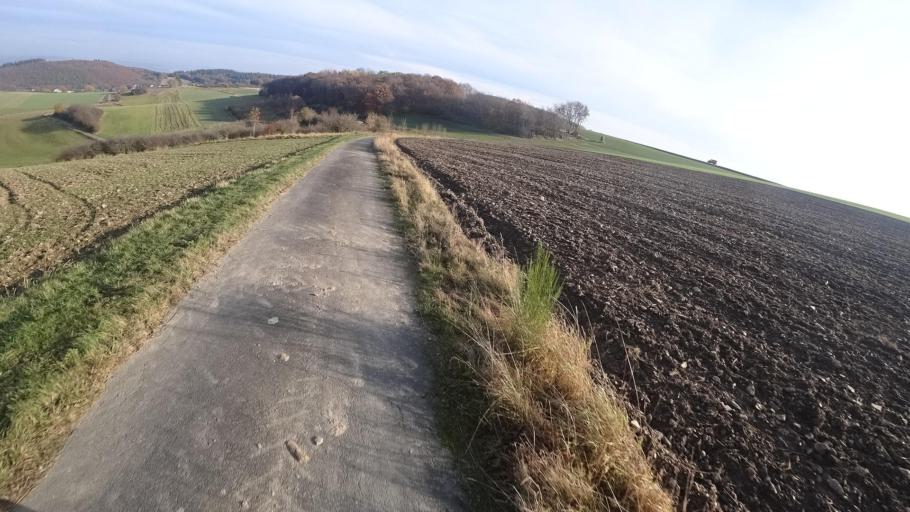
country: DE
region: Rheinland-Pfalz
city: Utzenhain
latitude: 50.1287
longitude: 7.6260
